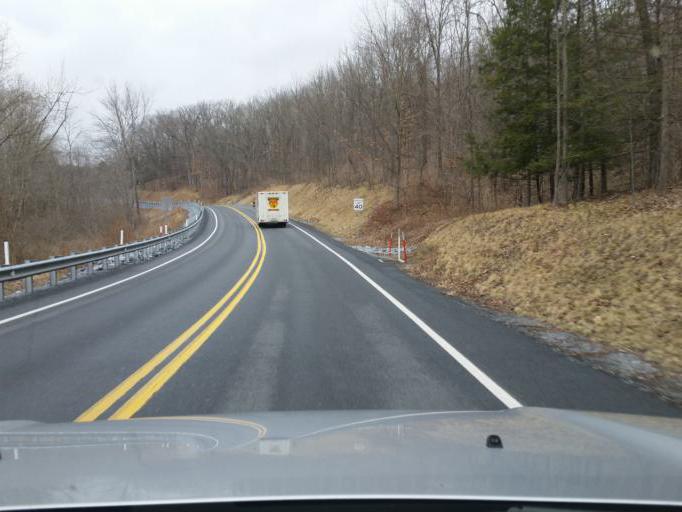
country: US
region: Pennsylvania
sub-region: Dauphin County
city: Rutherford
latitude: 40.2849
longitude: -76.7569
